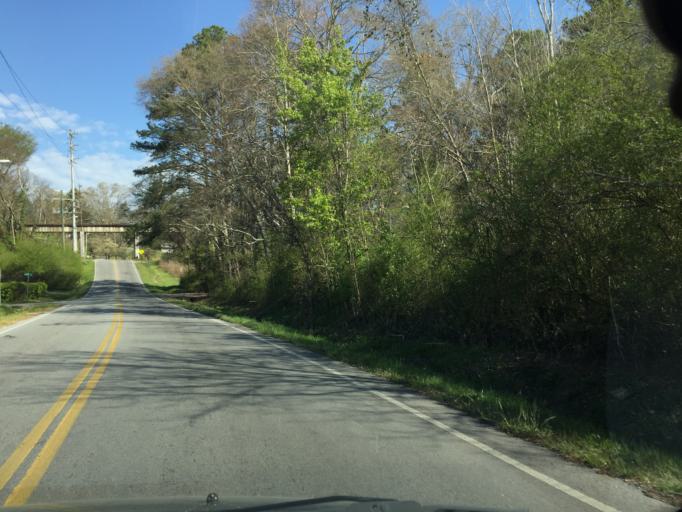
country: US
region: Tennessee
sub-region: Hamilton County
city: East Chattanooga
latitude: 35.0641
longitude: -85.2276
